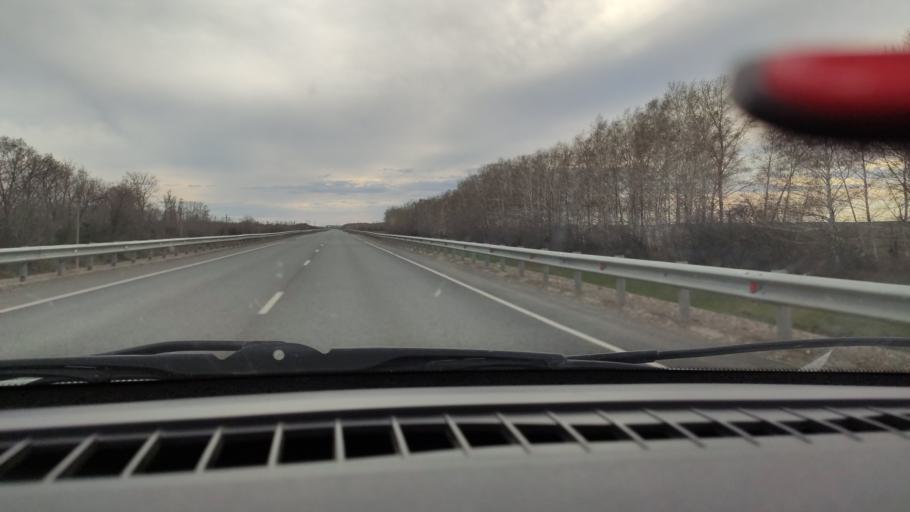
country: RU
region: Bashkortostan
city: Mayachnyy
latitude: 52.4050
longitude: 55.7251
